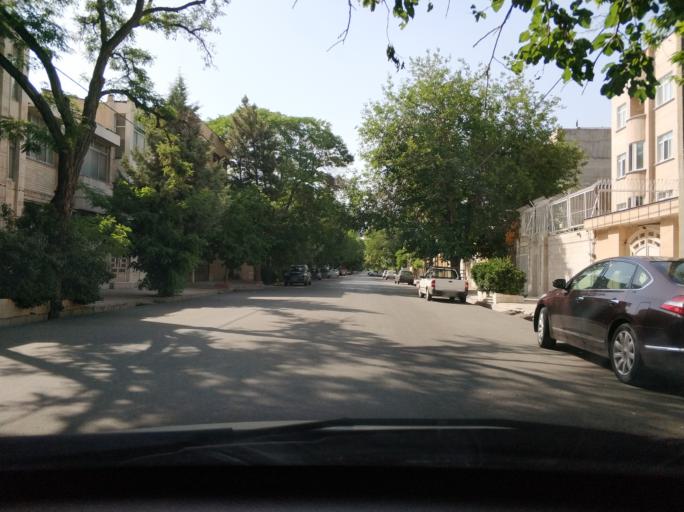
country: IR
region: Razavi Khorasan
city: Mashhad
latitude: 36.2712
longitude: 59.5987
